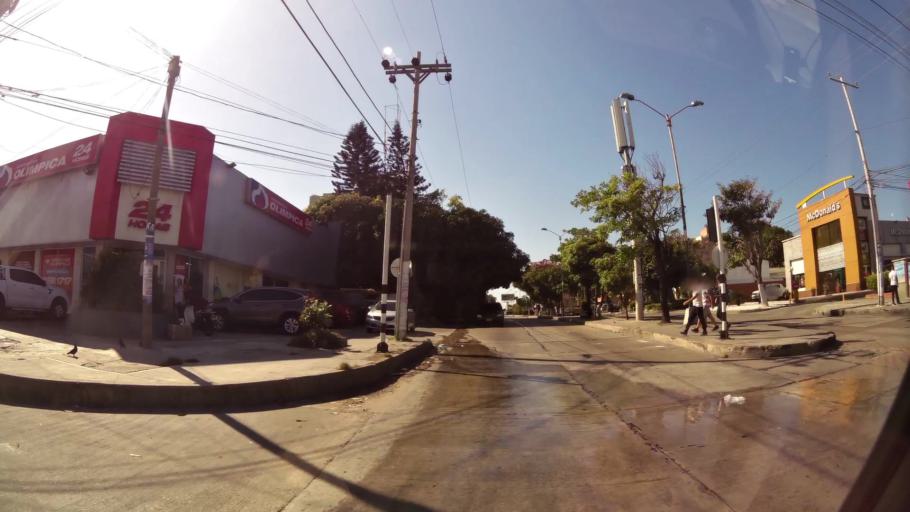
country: CO
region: Atlantico
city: Barranquilla
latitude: 11.0046
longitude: -74.8270
